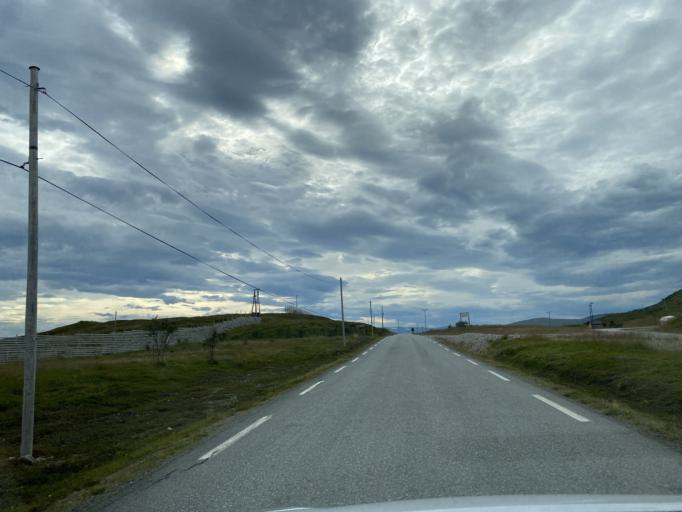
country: NO
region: Troms
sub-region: Karlsoy
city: Hansnes
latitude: 70.1003
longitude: 20.1061
